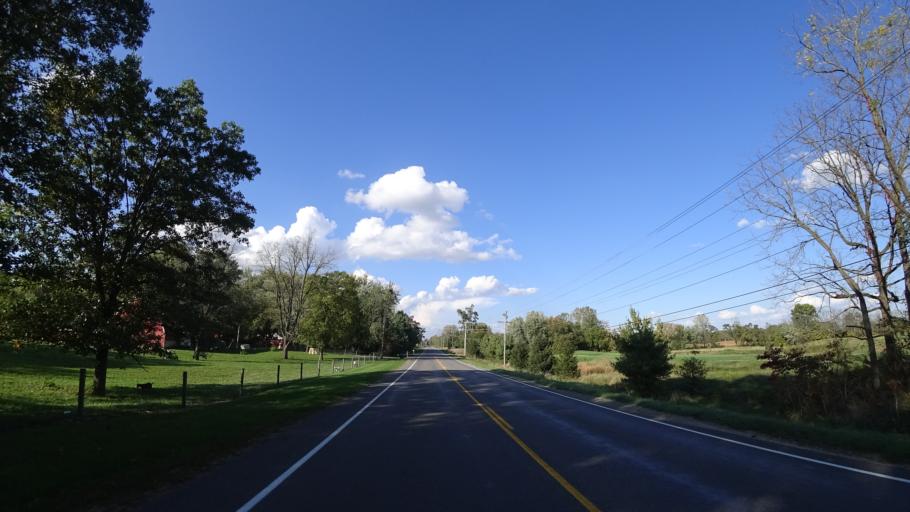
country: US
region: Michigan
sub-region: Saint Joseph County
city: Centreville
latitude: 41.9027
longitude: -85.5070
